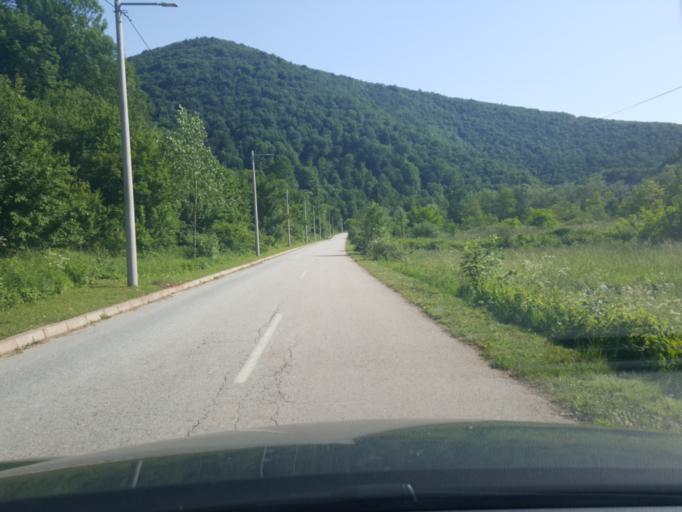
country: RS
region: Central Serbia
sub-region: Nisavski Okrug
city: Razanj
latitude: 43.8625
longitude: 21.6254
